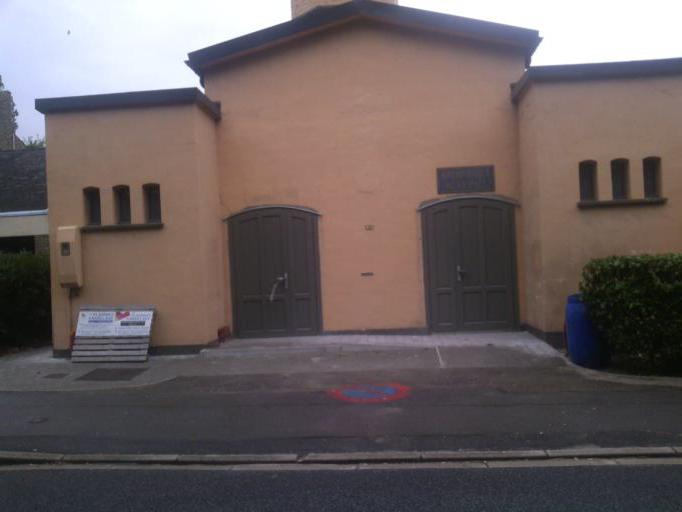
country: FR
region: Nord-Pas-de-Calais
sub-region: Departement du Nord
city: Hondschoote
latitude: 50.9789
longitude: 2.5859
